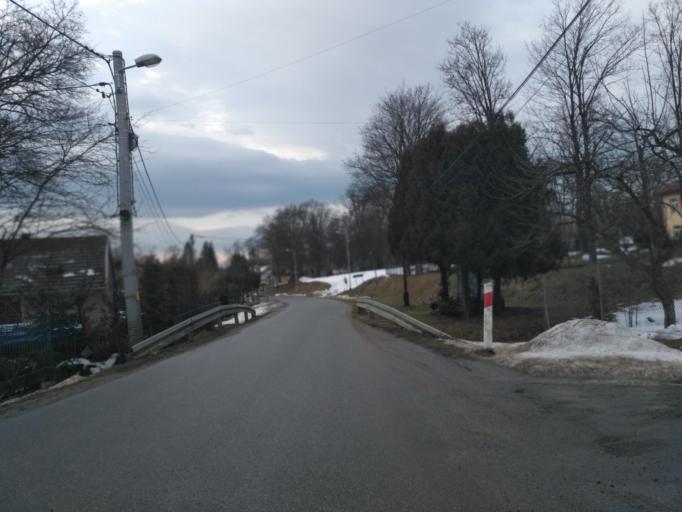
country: PL
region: Subcarpathian Voivodeship
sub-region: Powiat brzozowski
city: Dydnia
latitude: 49.6329
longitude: 22.1689
